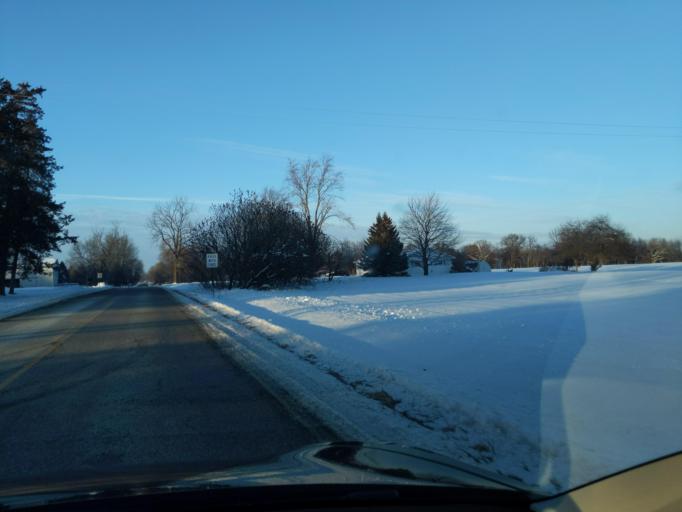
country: US
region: Michigan
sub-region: Ingham County
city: Stockbridge
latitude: 42.5401
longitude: -84.1125
